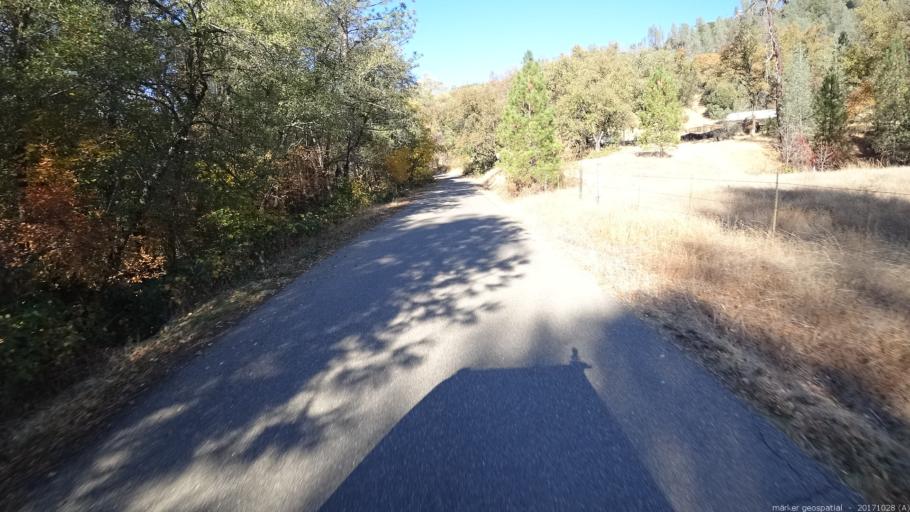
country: US
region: California
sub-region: Shasta County
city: Shasta
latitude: 40.7599
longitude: -122.6021
